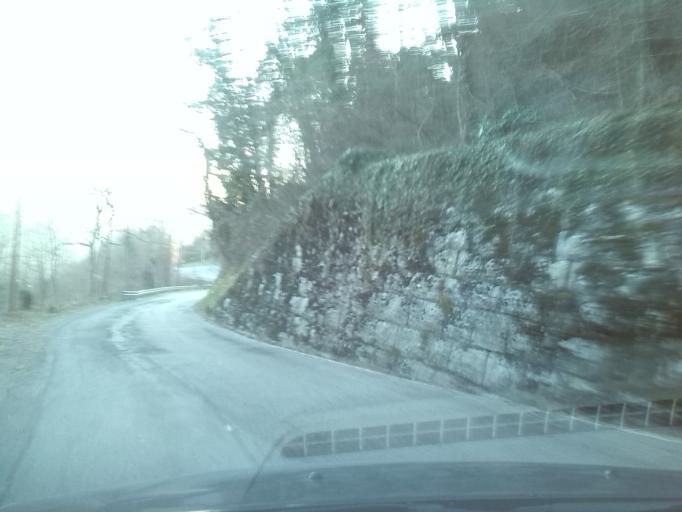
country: IT
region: Friuli Venezia Giulia
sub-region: Provincia di Udine
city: Clodig
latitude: 46.1785
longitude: 13.5692
